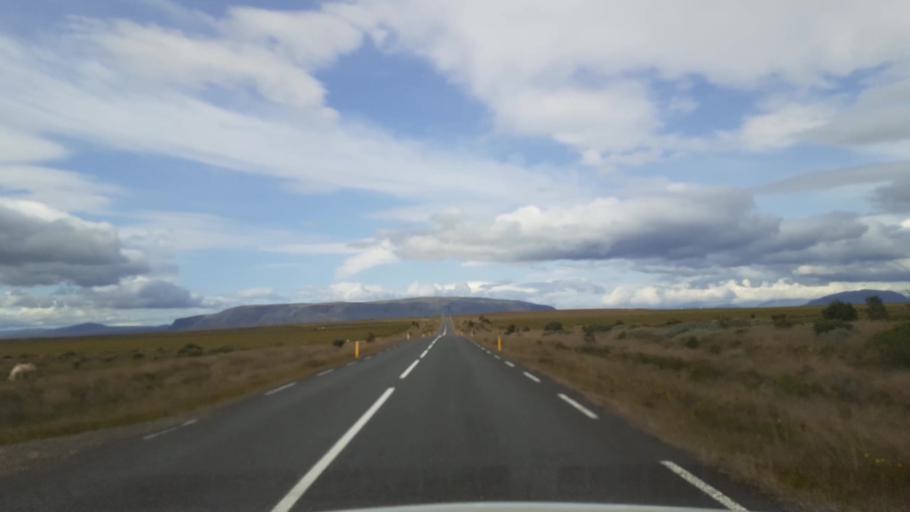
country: IS
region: South
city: Selfoss
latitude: 63.9133
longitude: -20.8341
